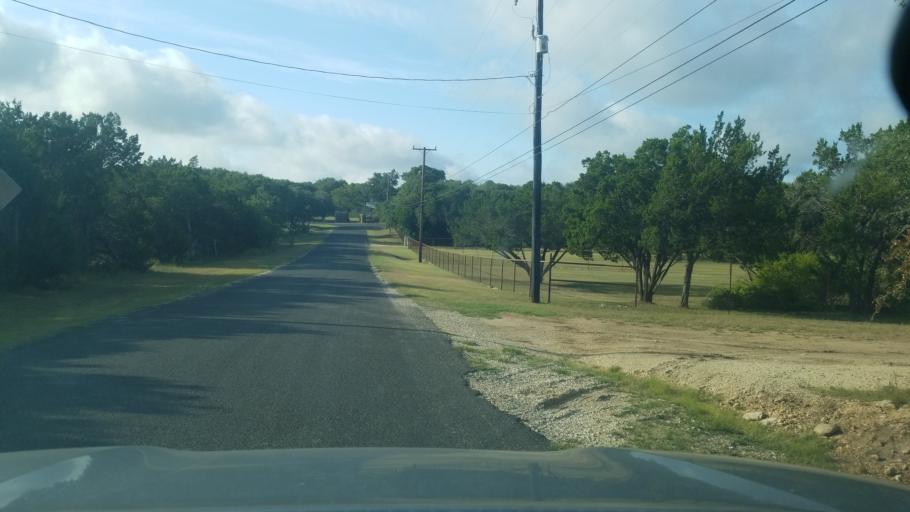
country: US
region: Texas
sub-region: Bexar County
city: Timberwood Park
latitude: 29.6965
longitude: -98.5154
